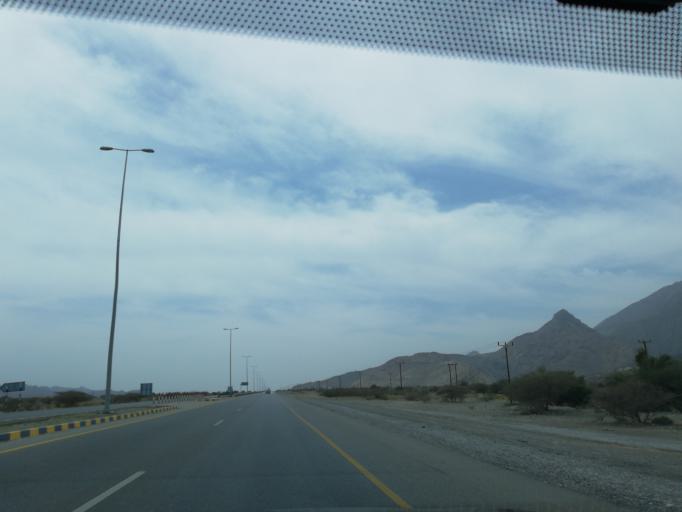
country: OM
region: Muhafazat ad Dakhiliyah
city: Izki
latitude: 23.0856
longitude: 57.8215
